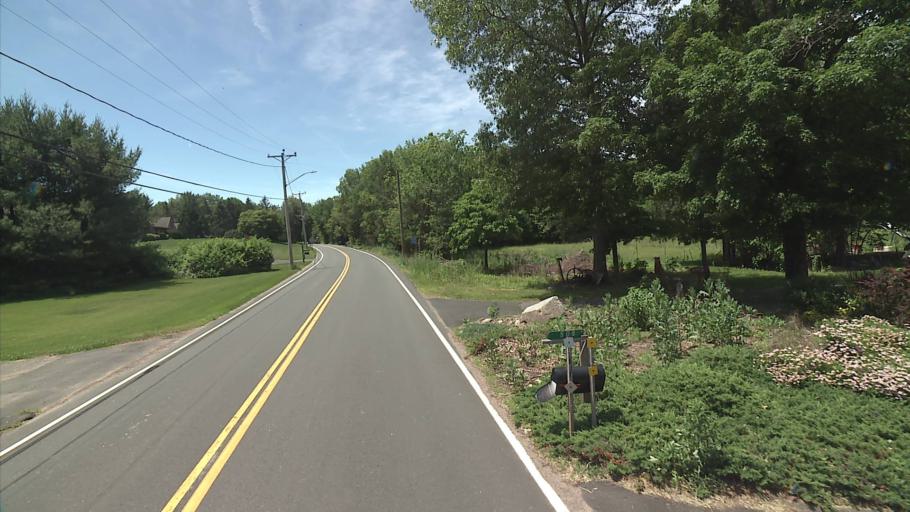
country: US
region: Connecticut
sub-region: New Haven County
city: Meriden
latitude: 41.5962
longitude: -72.8260
